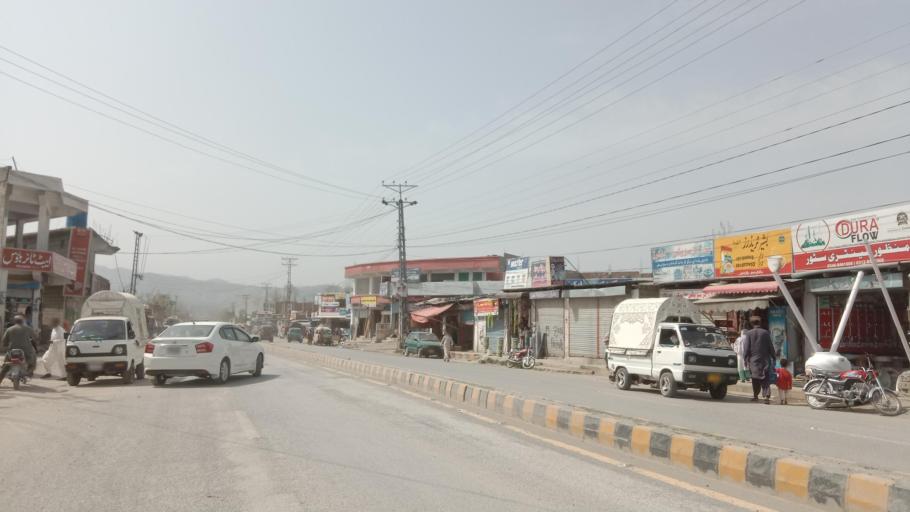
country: PK
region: Khyber Pakhtunkhwa
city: Abbottabad
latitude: 34.1578
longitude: 73.2594
